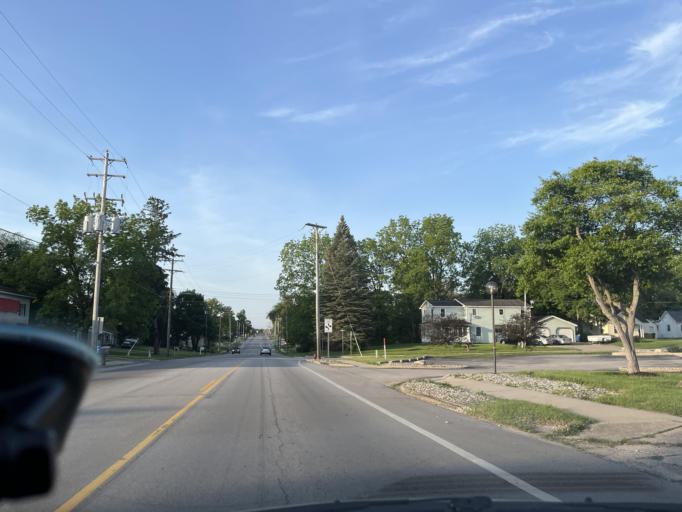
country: US
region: Michigan
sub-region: Barry County
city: Middleville
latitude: 42.7135
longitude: -85.4701
